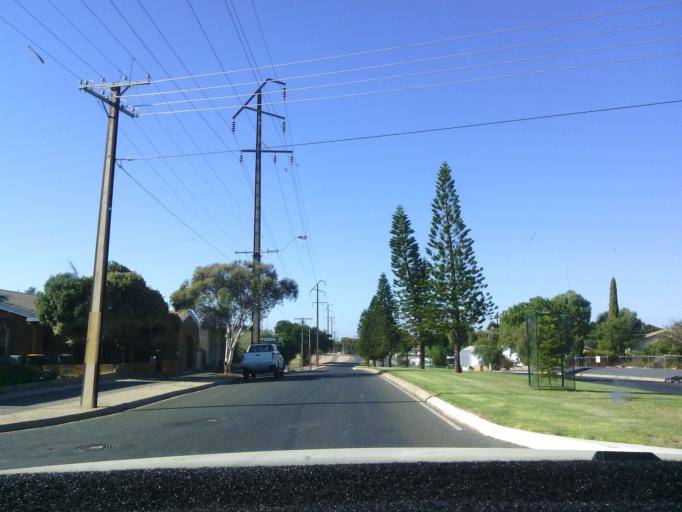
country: AU
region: South Australia
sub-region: Berri and Barmera
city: Berri
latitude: -34.2779
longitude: 140.5973
